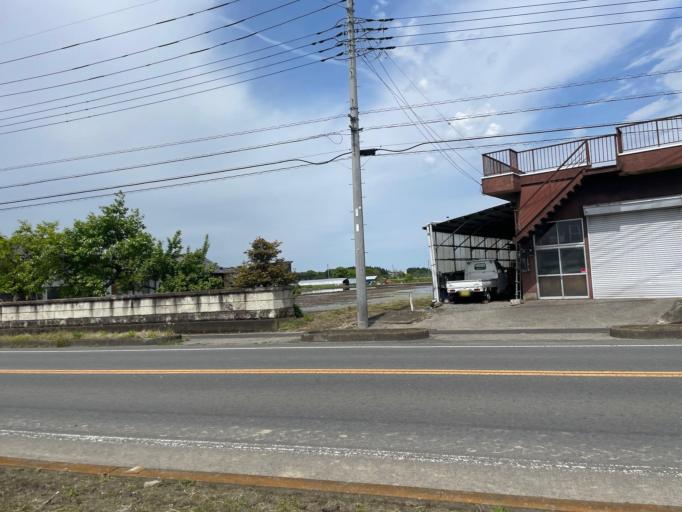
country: JP
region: Tochigi
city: Mibu
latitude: 36.4657
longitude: 139.7672
